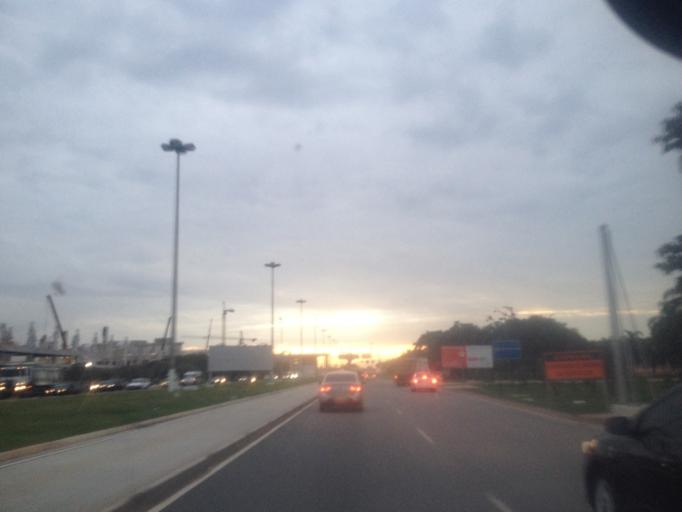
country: BR
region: Rio de Janeiro
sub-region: Duque De Caxias
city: Duque de Caxias
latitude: -22.8166
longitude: -43.2401
